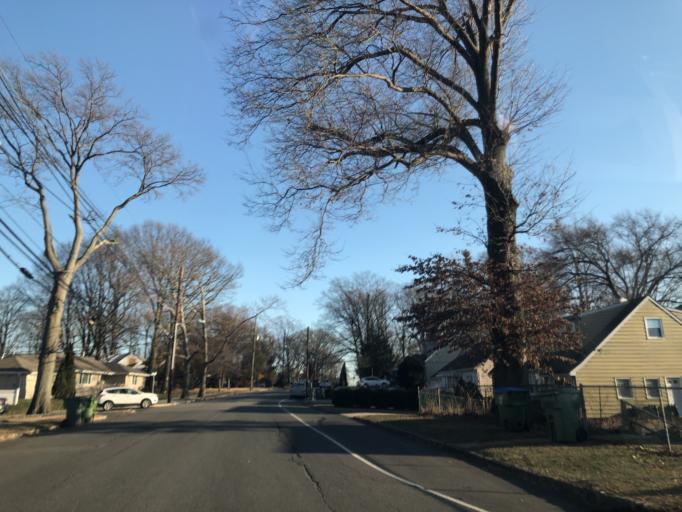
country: US
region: New Jersey
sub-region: Middlesex County
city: Fords
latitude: 40.5383
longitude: -74.3331
